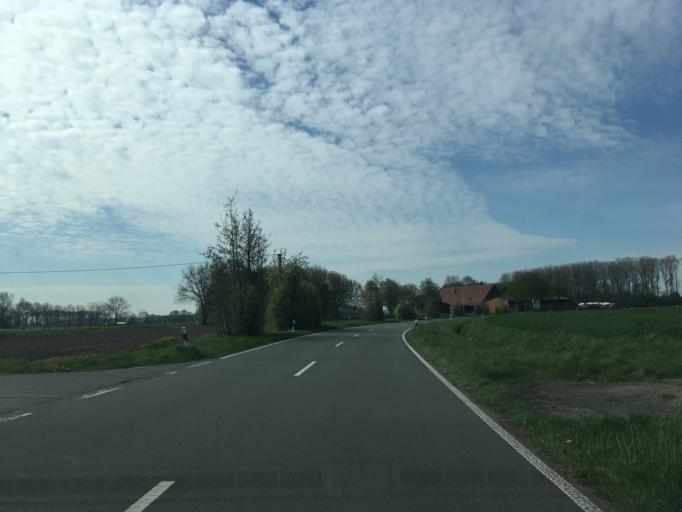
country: DE
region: North Rhine-Westphalia
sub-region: Regierungsbezirk Munster
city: Borken
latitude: 51.8783
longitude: 6.8047
